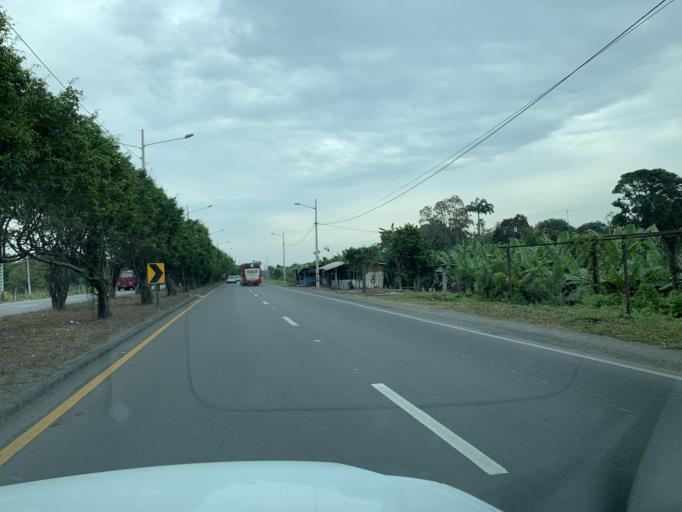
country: EC
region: Guayas
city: Yaguachi Nuevo
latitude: -2.2349
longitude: -79.6507
